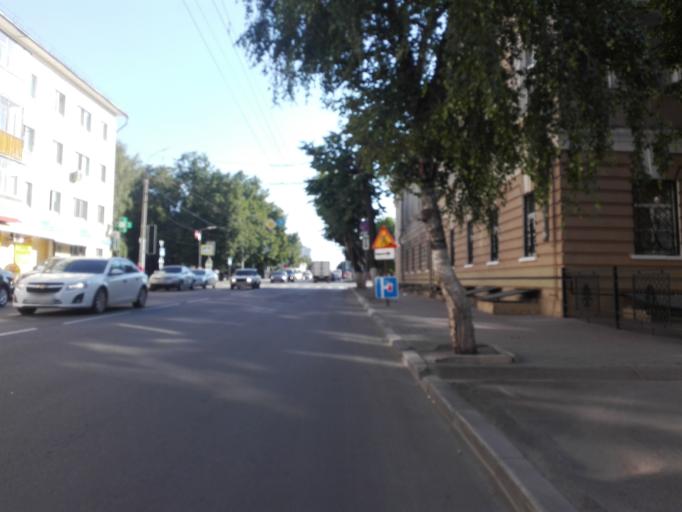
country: RU
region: Orjol
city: Orel
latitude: 52.9766
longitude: 36.0644
